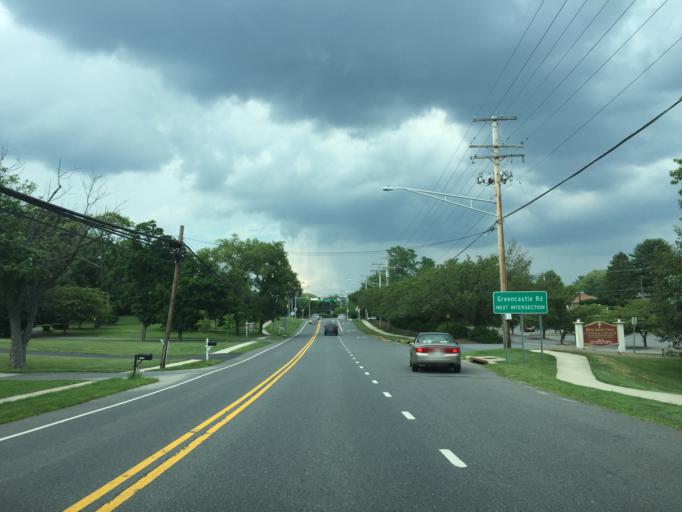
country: US
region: Maryland
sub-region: Montgomery County
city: Burtonsville
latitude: 39.0970
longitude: -76.9452
